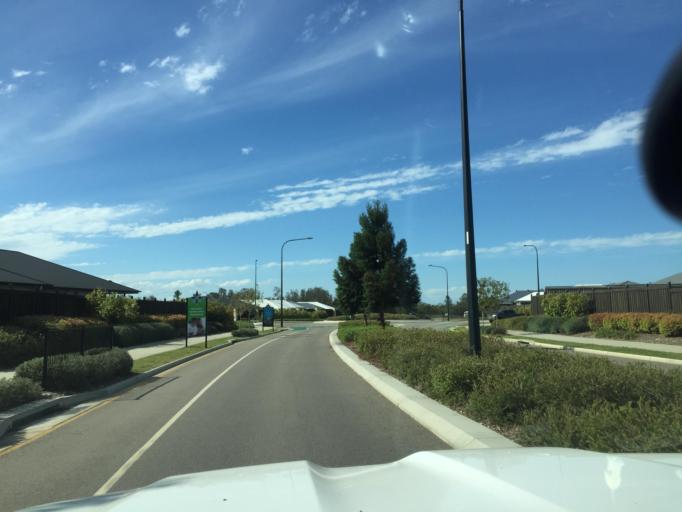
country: AU
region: Queensland
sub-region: Moreton Bay
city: Morayfield
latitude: -27.1189
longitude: 152.9936
